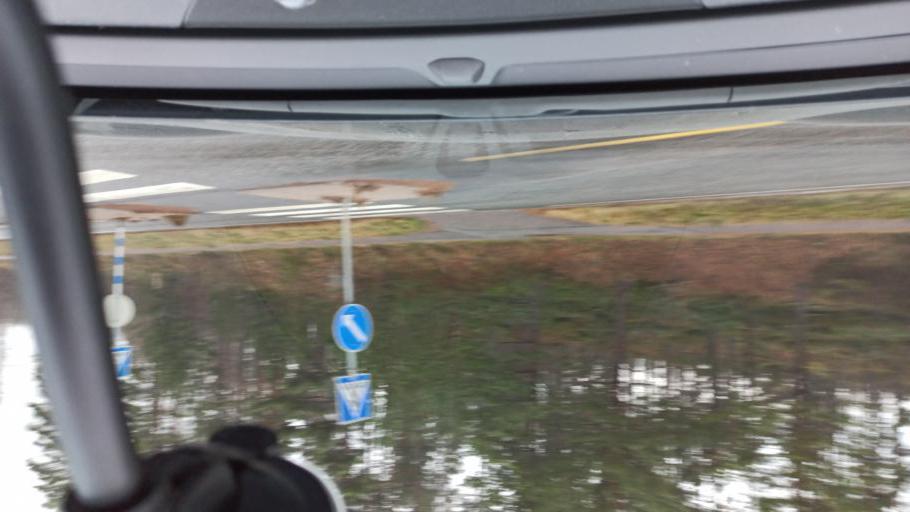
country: FI
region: Uusimaa
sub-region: Helsinki
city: Kirkkonummi
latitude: 60.1304
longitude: 24.4836
